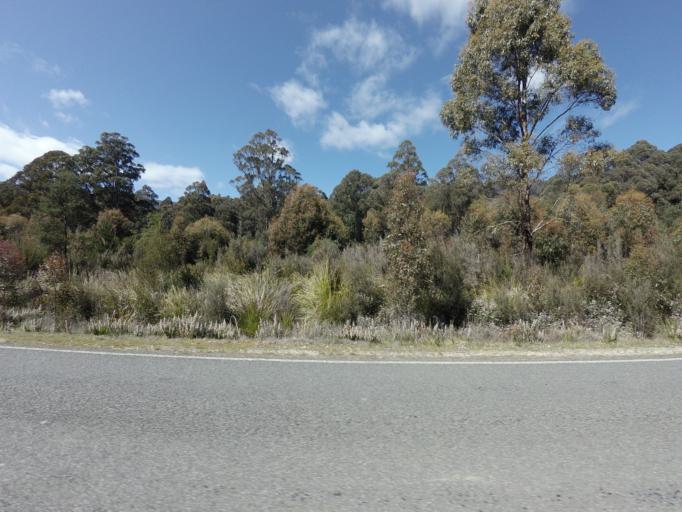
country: AU
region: Tasmania
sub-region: Derwent Valley
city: New Norfolk
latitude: -42.7196
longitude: 146.6848
